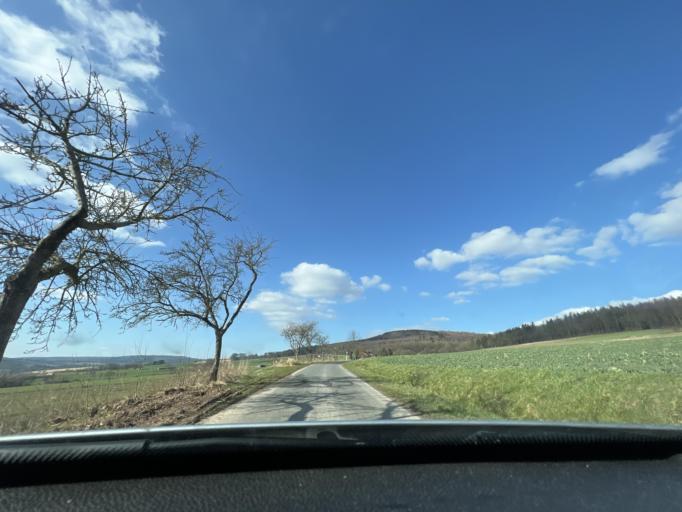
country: DE
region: Lower Saxony
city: Uslar
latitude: 51.6773
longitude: 9.6133
